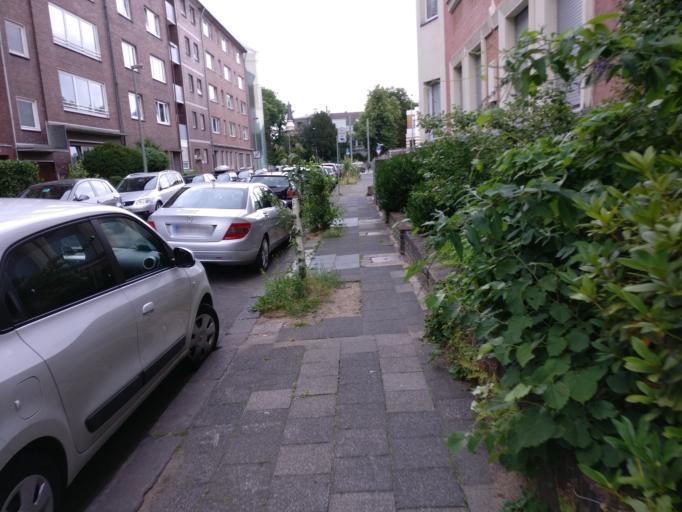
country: DE
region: North Rhine-Westphalia
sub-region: Regierungsbezirk Dusseldorf
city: Duisburg
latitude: 51.4321
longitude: 6.7890
